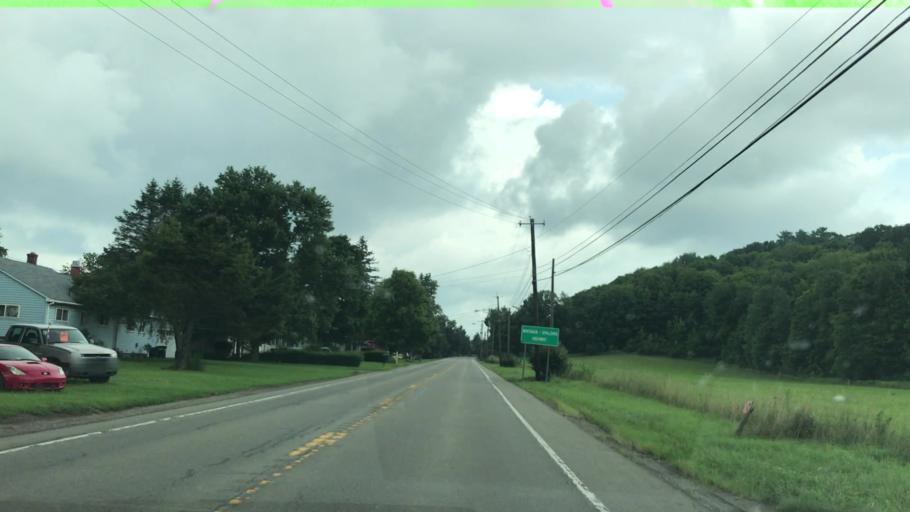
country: US
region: New York
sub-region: Steuben County
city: Bath
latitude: 42.3802
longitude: -77.3613
